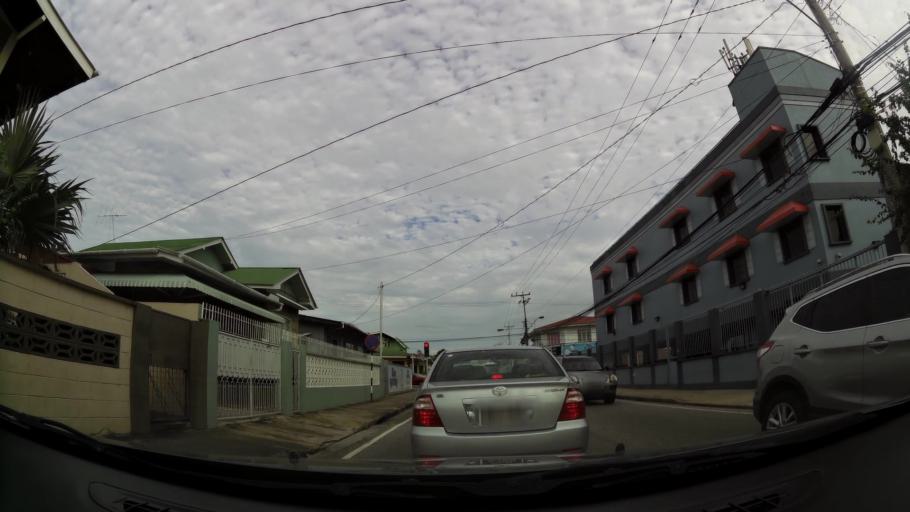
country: TT
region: City of Port of Spain
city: Port-of-Spain
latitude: 10.6657
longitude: -61.5267
